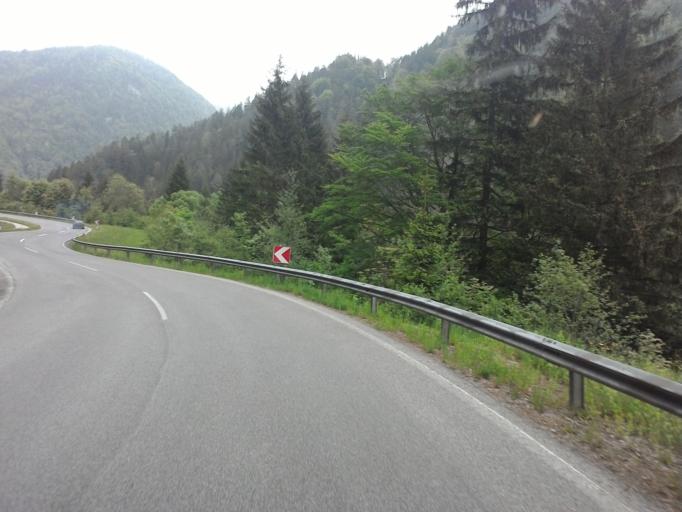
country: AT
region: Styria
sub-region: Politischer Bezirk Liezen
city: Landl
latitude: 47.6634
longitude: 14.7310
